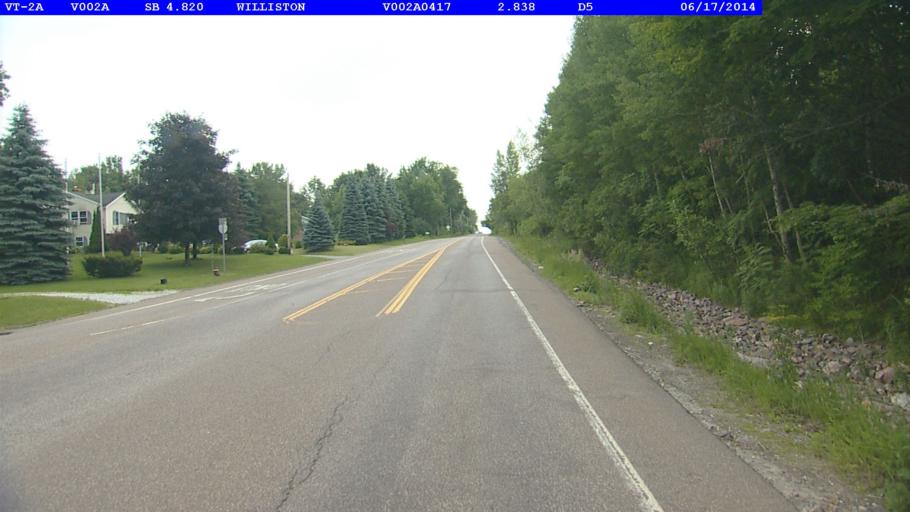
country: US
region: Vermont
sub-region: Chittenden County
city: Williston
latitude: 44.4376
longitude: -73.1161
